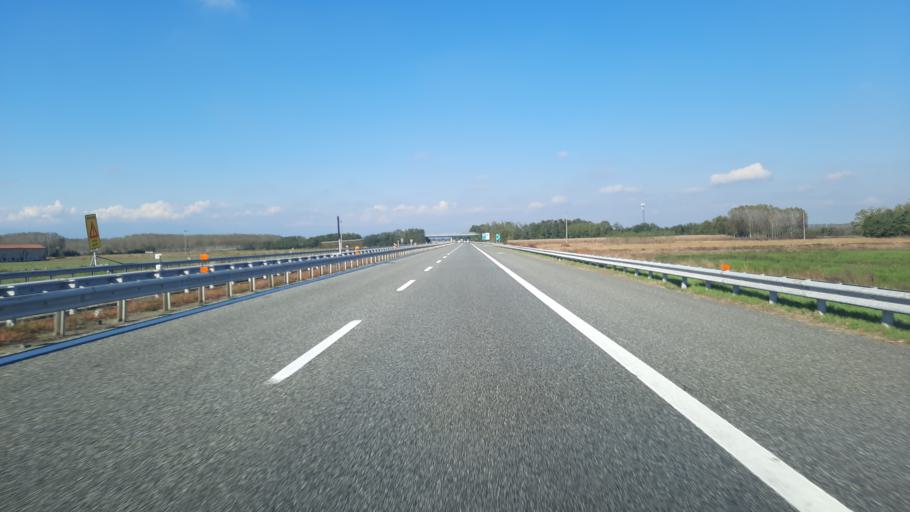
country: IT
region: Piedmont
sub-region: Provincia di Novara
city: Mandello Vitta
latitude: 45.4910
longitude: 8.4414
